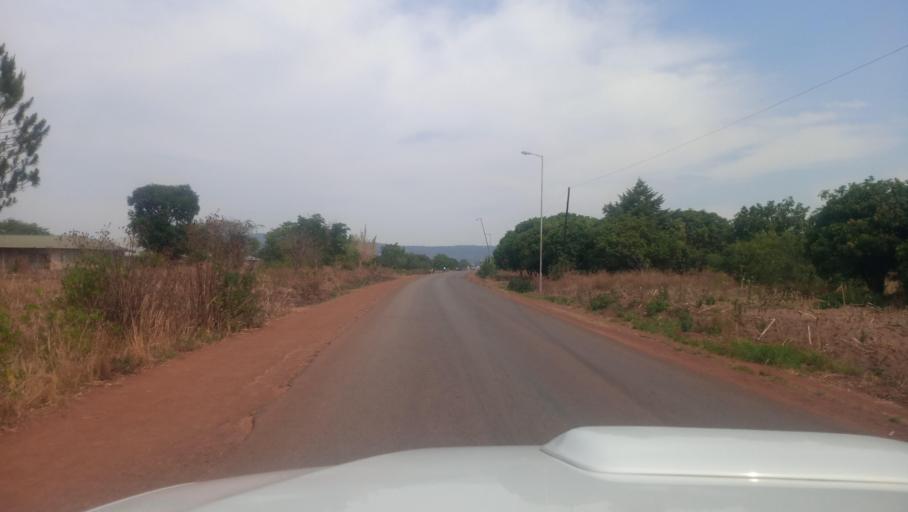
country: ZM
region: Northern
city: Mpika
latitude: -11.8341
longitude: 31.4252
